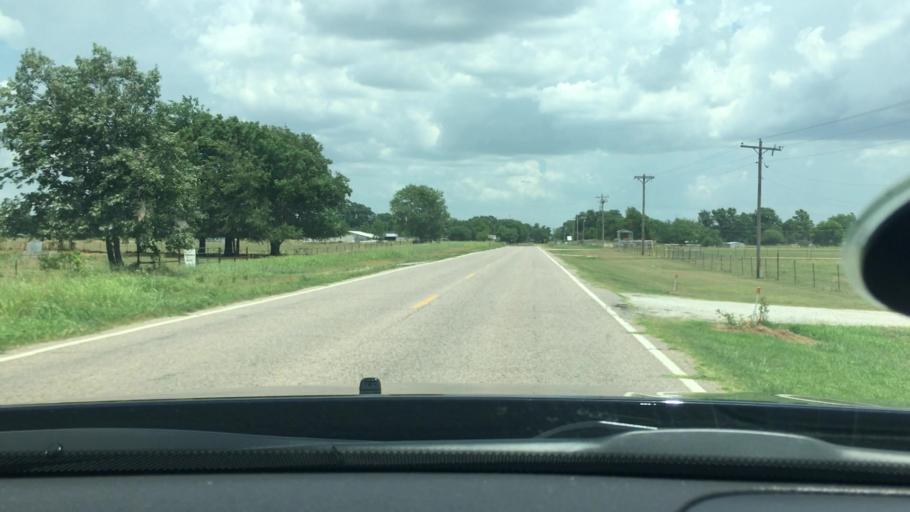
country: US
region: Texas
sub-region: Grayson County
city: Sherwood Shores
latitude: 33.9839
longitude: -96.9196
